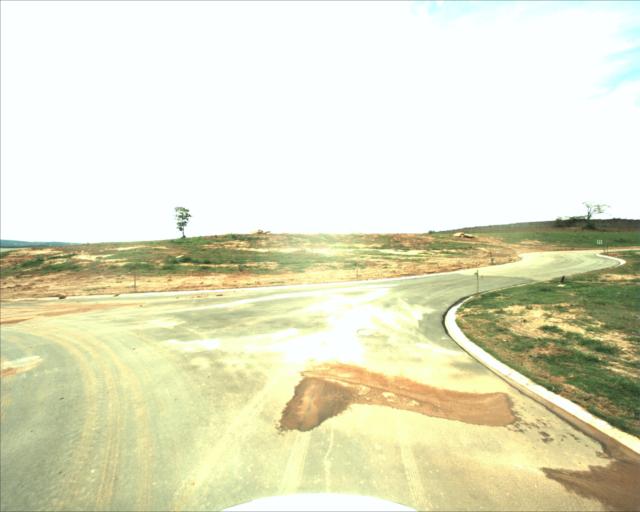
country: BR
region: Sao Paulo
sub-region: Votorantim
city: Votorantim
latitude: -23.5747
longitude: -47.5060
